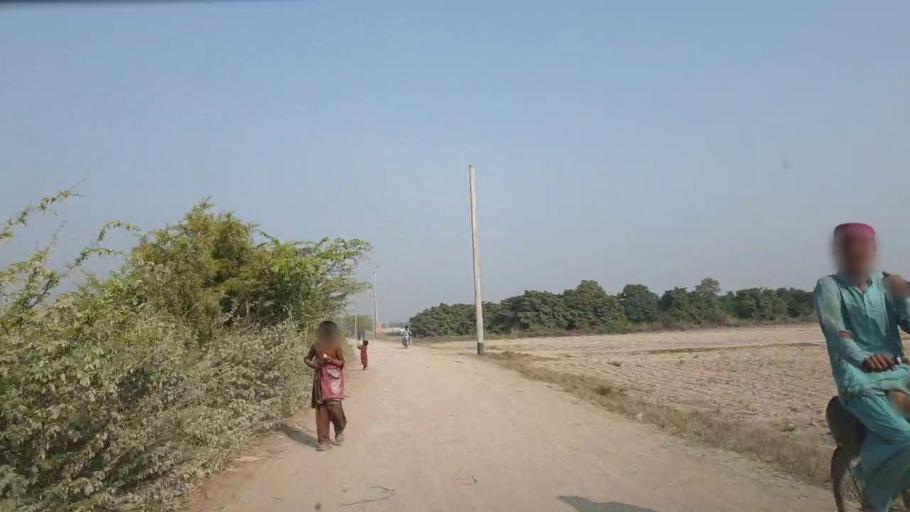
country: PK
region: Sindh
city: Mirpur Khas
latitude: 25.5467
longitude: 69.0211
